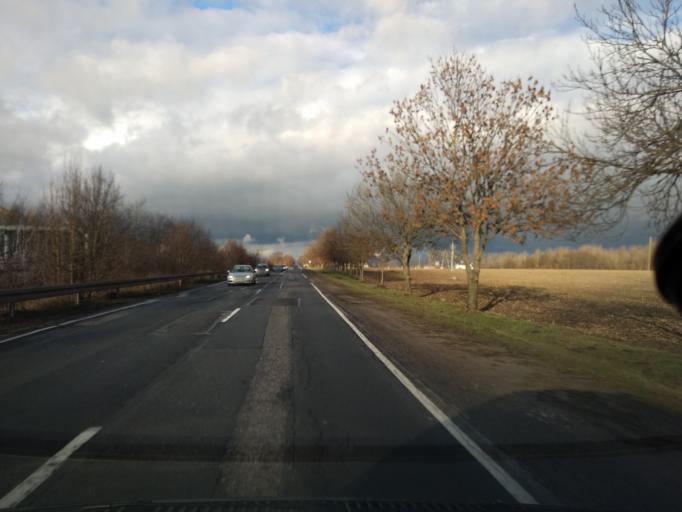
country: PL
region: Greater Poland Voivodeship
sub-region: Konin
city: Konin
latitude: 52.2569
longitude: 18.2686
